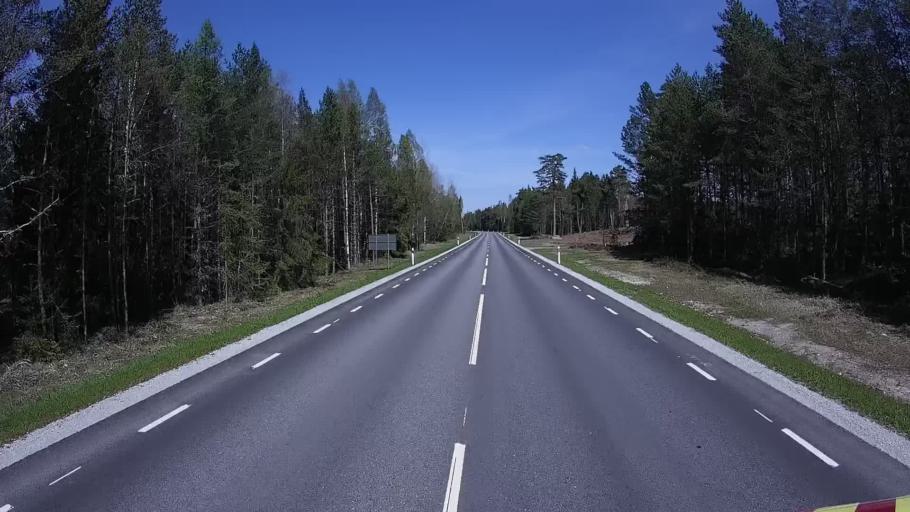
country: EE
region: Harju
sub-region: Nissi vald
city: Turba
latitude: 59.1337
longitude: 24.0736
